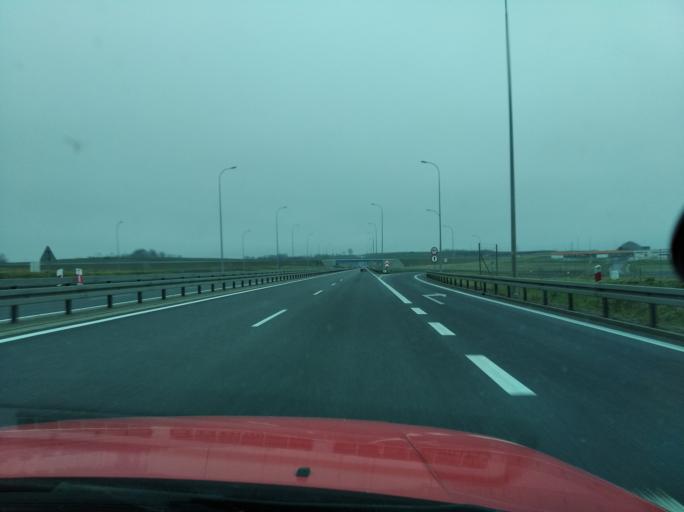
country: PL
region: Subcarpathian Voivodeship
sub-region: Powiat jaroslawski
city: Wierzbna
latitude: 50.0366
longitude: 22.5801
